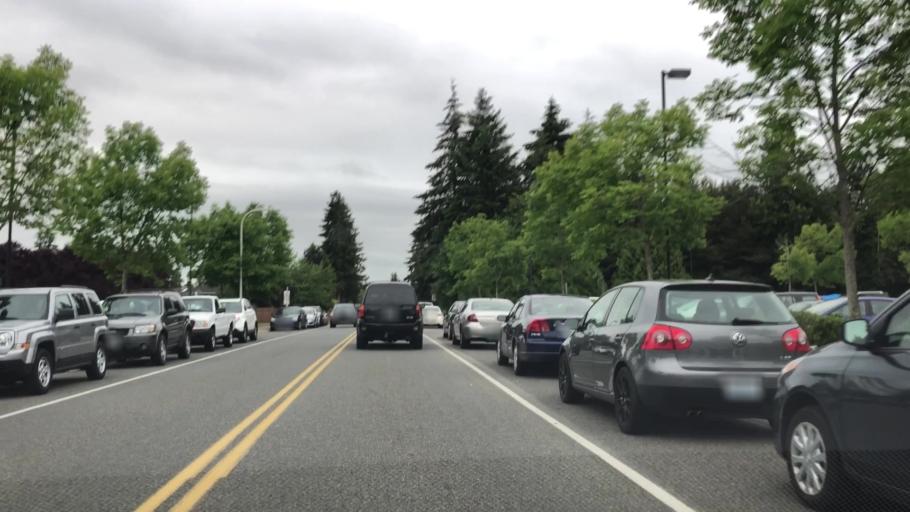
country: US
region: Washington
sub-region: Snohomish County
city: Mill Creek
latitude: 47.8742
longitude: -122.2044
